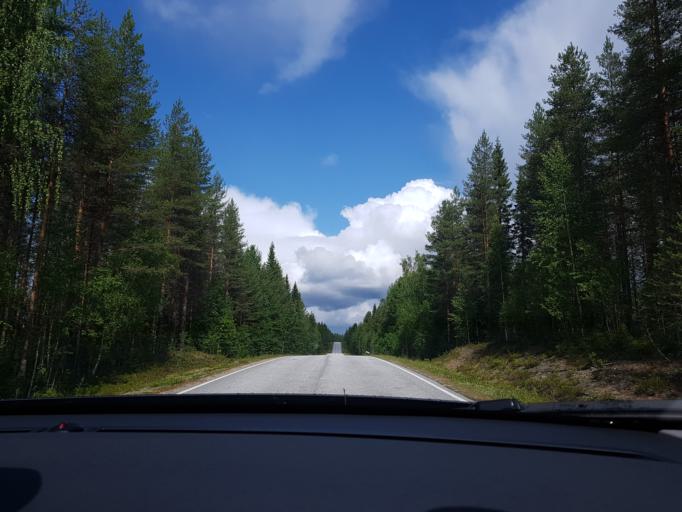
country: FI
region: Kainuu
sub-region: Kehys-Kainuu
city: Kuhmo
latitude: 64.4275
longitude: 29.4989
